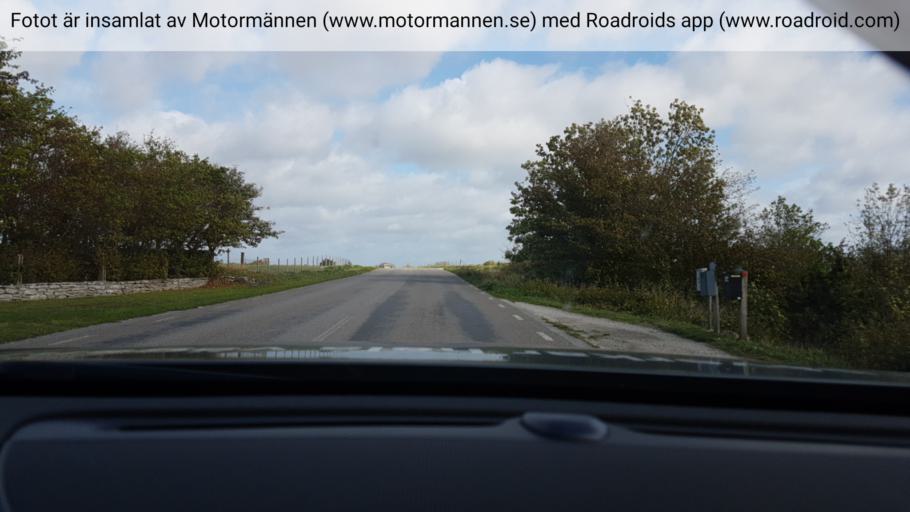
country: SE
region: Gotland
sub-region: Gotland
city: Slite
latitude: 57.9216
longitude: 19.1403
